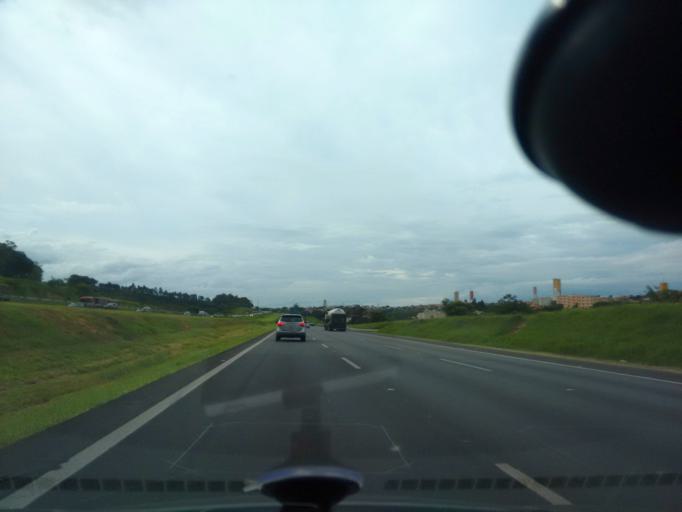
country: BR
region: Sao Paulo
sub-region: Campinas
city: Campinas
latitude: -22.9515
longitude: -47.1256
